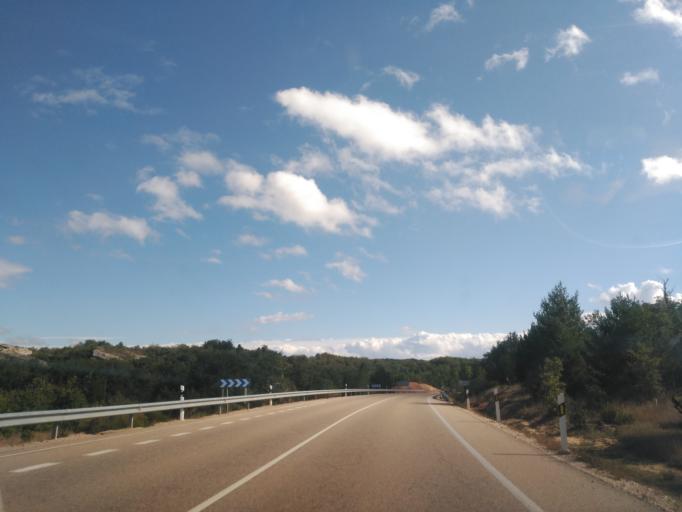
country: ES
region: Castille and Leon
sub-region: Provincia de Burgos
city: Pinilla de los Barruecos
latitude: 41.9259
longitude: -3.2799
